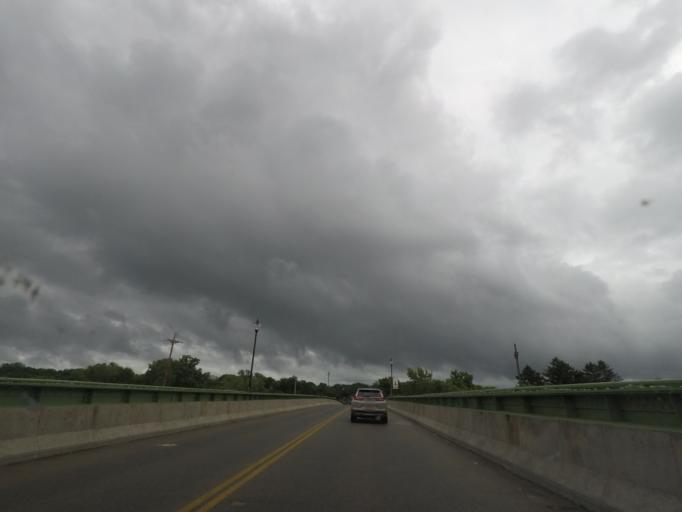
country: US
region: New York
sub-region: Rensselaer County
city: Rensselaer
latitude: 42.6376
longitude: -73.7429
